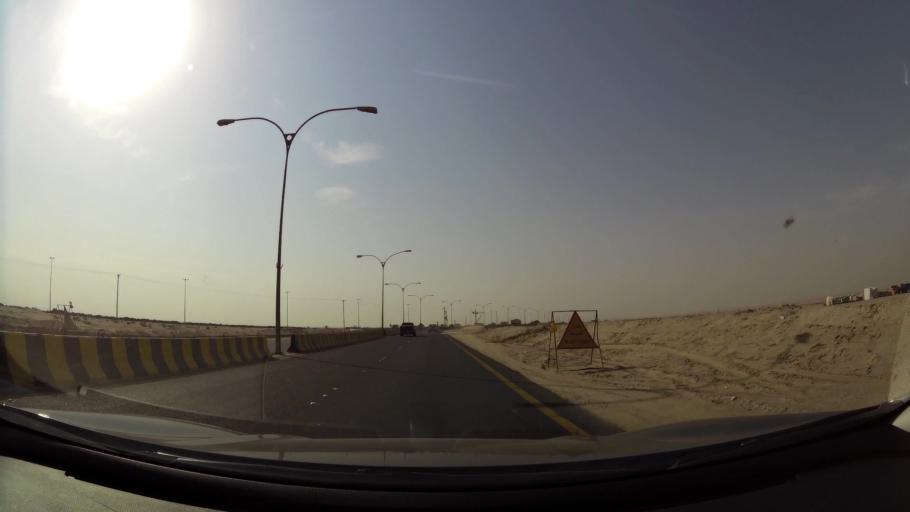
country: KW
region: Al Ahmadi
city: Al Ahmadi
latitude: 28.8923
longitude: 48.0850
